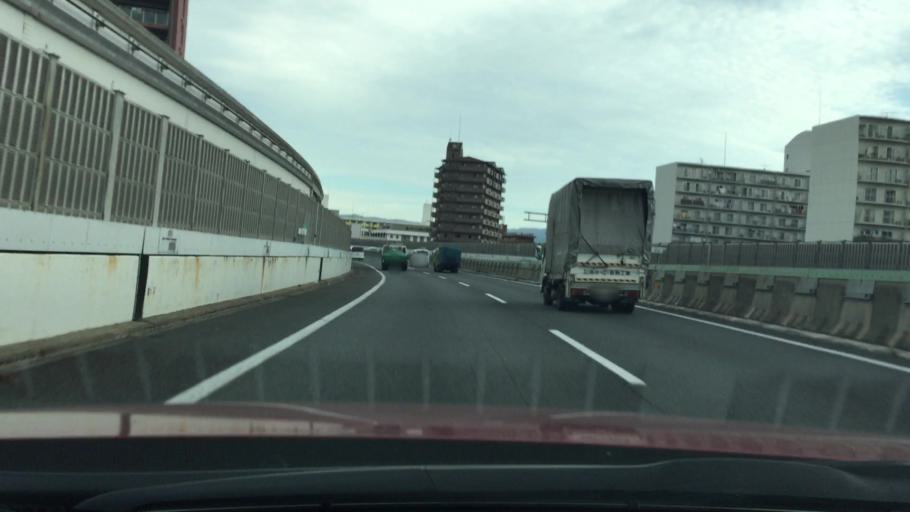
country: JP
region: Osaka
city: Ibaraki
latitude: 34.7984
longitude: 135.5669
